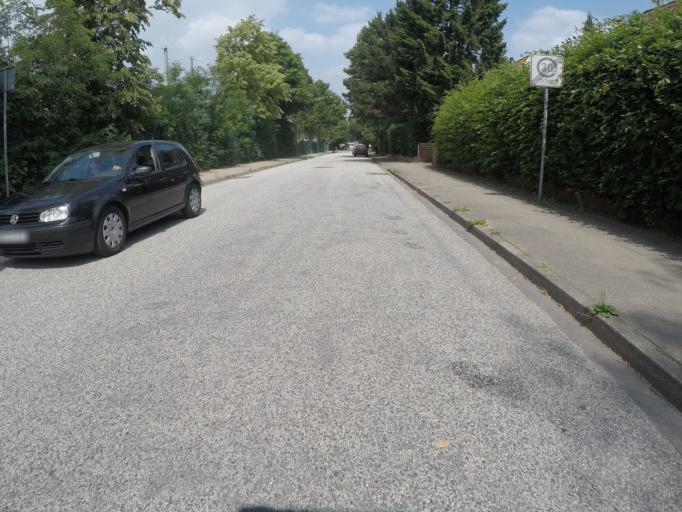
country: DE
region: Hamburg
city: Eidelstedt
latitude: 53.5815
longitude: 9.8727
